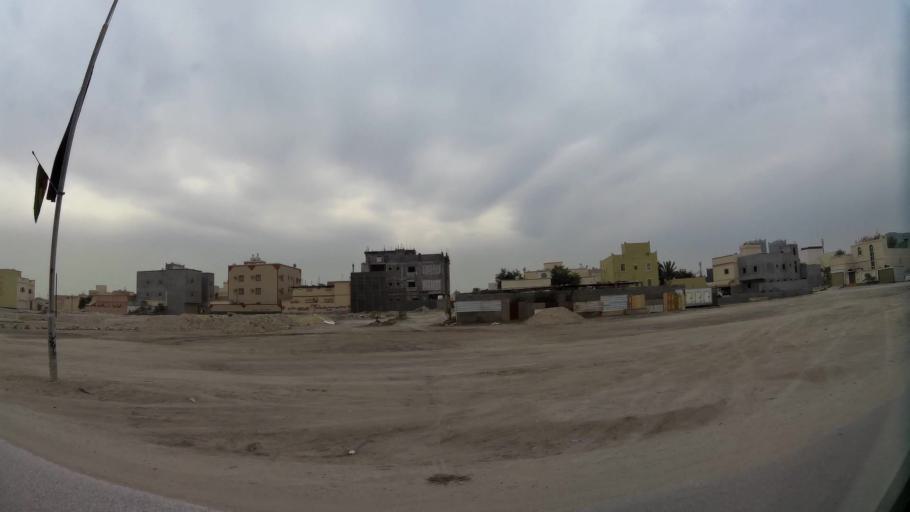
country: BH
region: Northern
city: Sitrah
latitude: 26.1422
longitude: 50.6091
